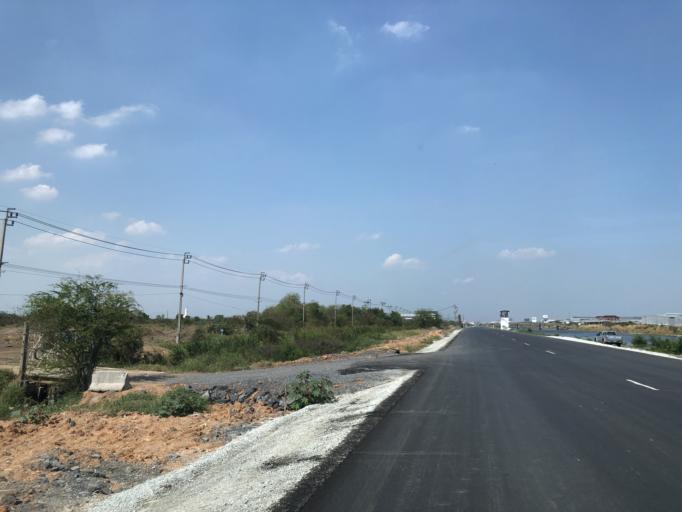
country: TH
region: Samut Prakan
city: Bang Bo District
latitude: 13.5502
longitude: 100.7523
